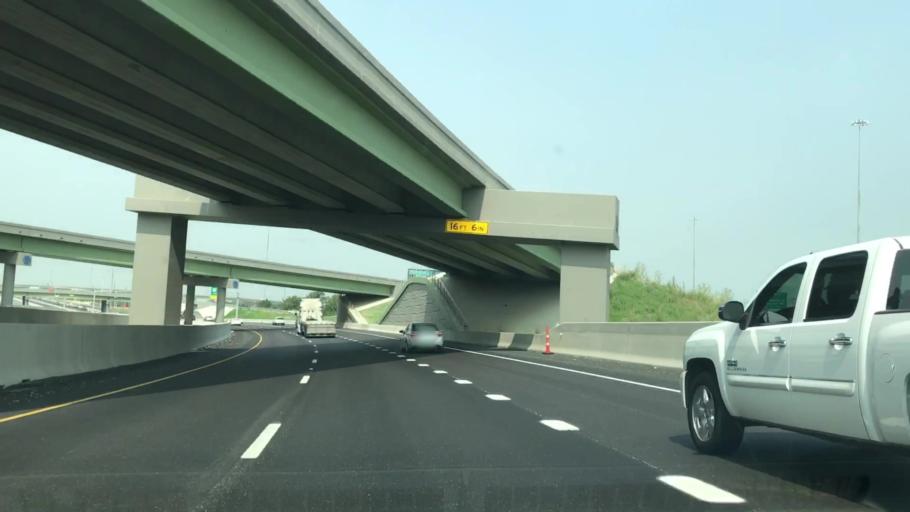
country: US
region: Texas
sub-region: Dallas County
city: Irving
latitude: 32.8345
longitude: -96.9039
